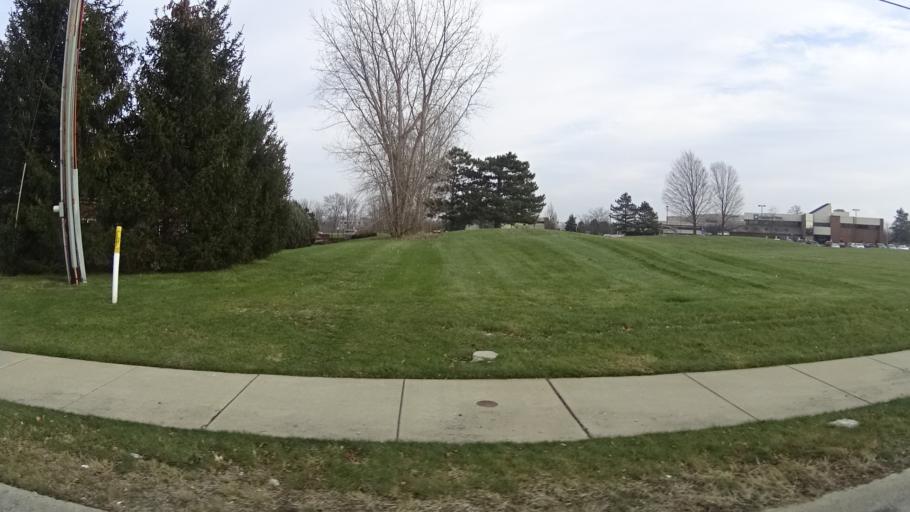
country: US
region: Ohio
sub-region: Lorain County
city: Amherst
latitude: 41.4137
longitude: -82.2389
